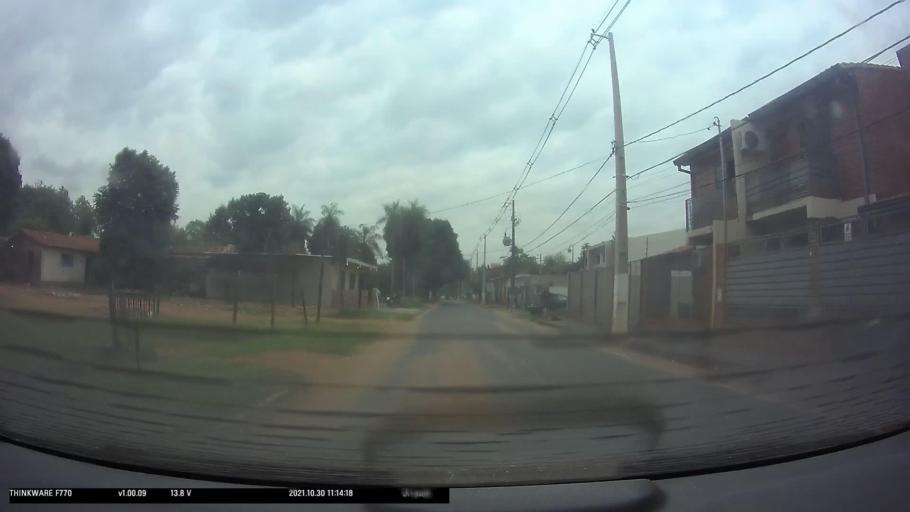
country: PY
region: Central
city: San Lorenzo
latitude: -25.3108
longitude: -57.5113
